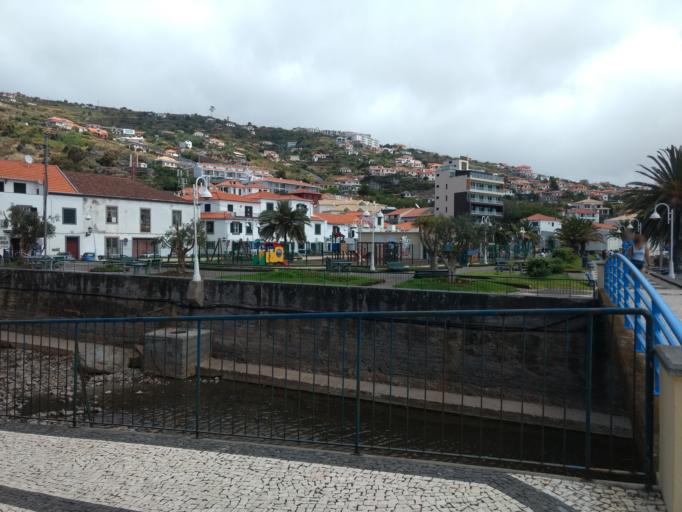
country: PT
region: Madeira
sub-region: Santa Cruz
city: Santa Cruz
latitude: 32.6867
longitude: -16.7918
